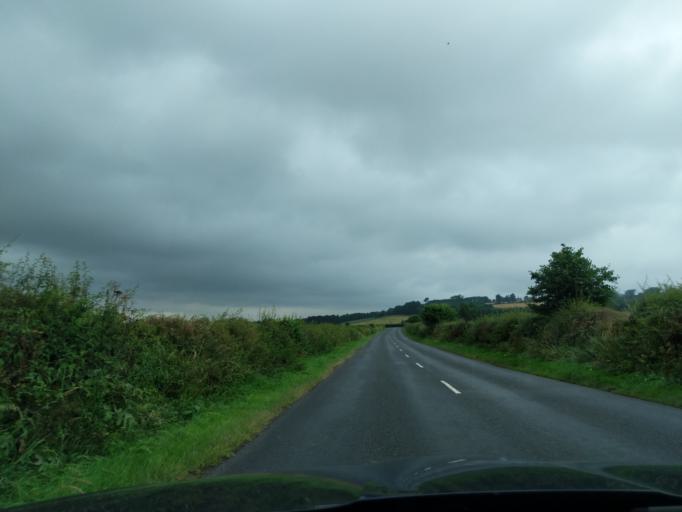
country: GB
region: England
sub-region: Northumberland
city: Ford
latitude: 55.6358
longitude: -2.1016
